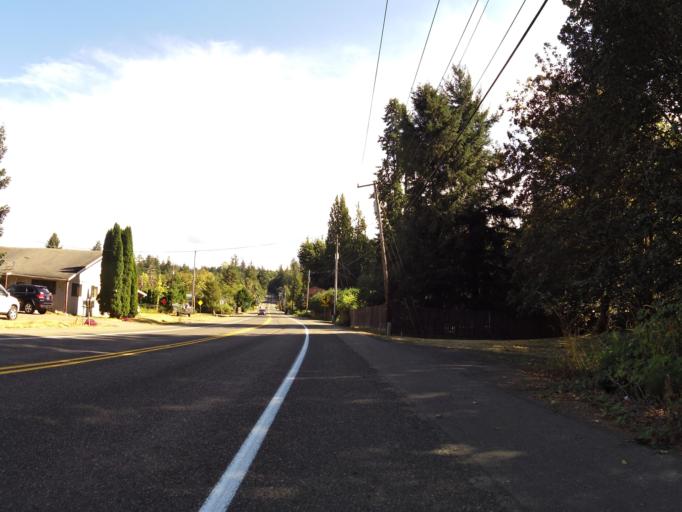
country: US
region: Washington
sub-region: Mason County
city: Shelton
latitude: 47.1283
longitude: -123.0968
